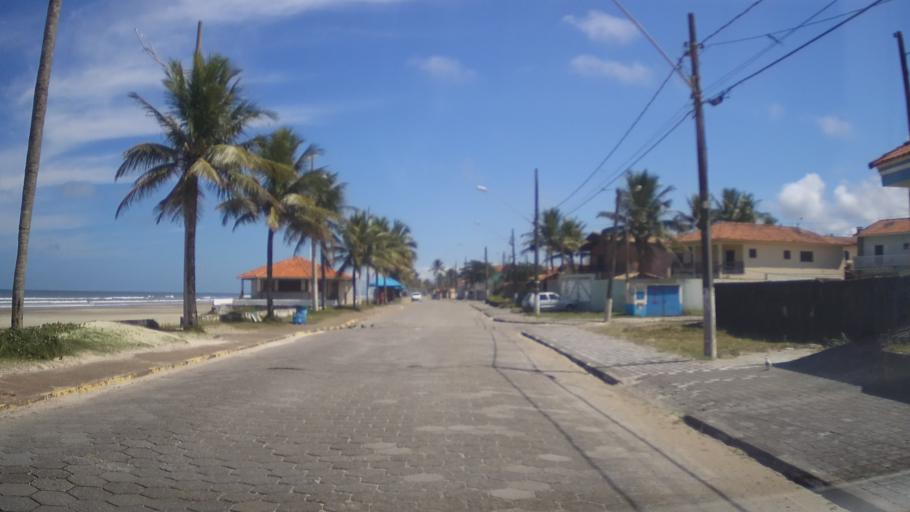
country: BR
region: Sao Paulo
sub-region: Mongagua
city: Mongagua
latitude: -24.1379
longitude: -46.7011
